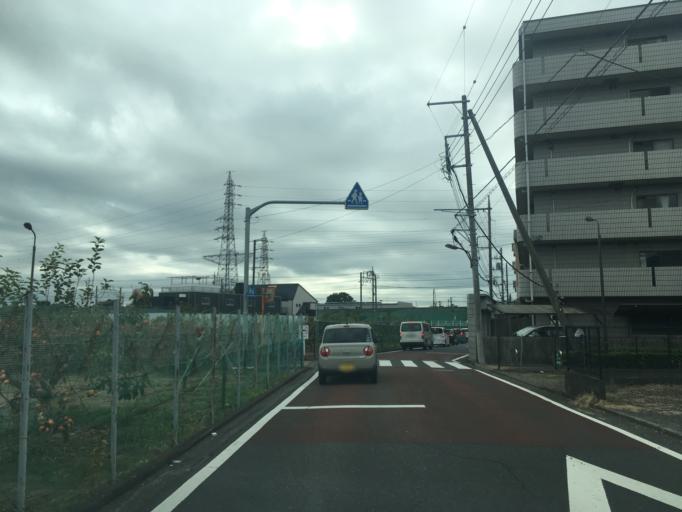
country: JP
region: Tokyo
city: Hino
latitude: 35.7293
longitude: 139.3860
